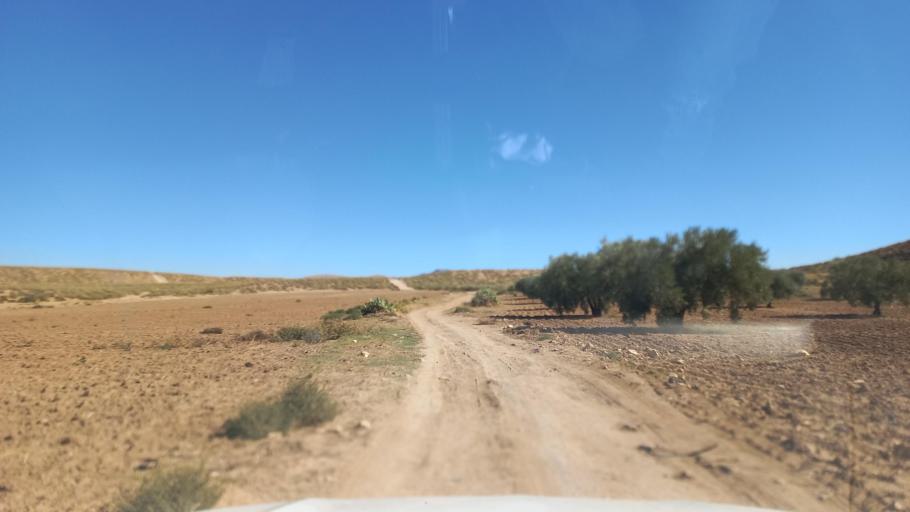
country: TN
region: Al Qasrayn
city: Sbiba
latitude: 35.4052
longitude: 9.0908
